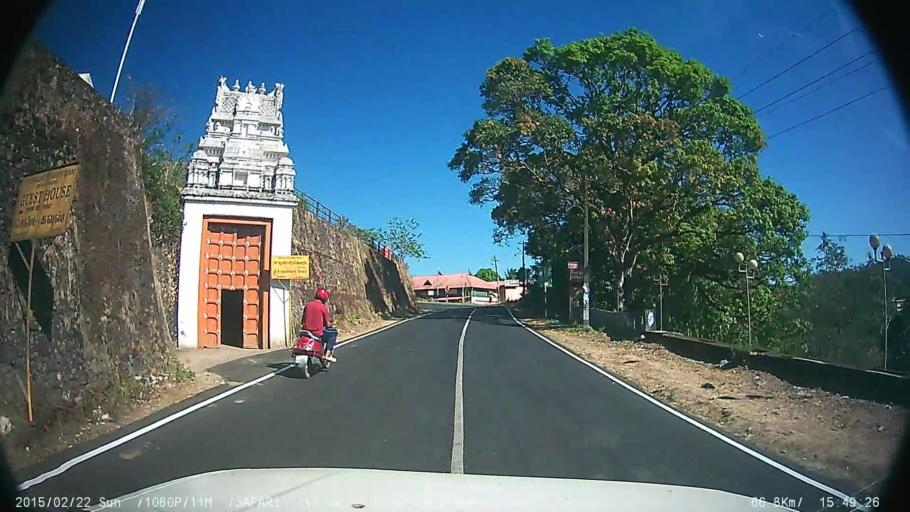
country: IN
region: Kerala
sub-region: Kottayam
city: Erattupetta
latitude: 9.5705
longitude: 76.9970
